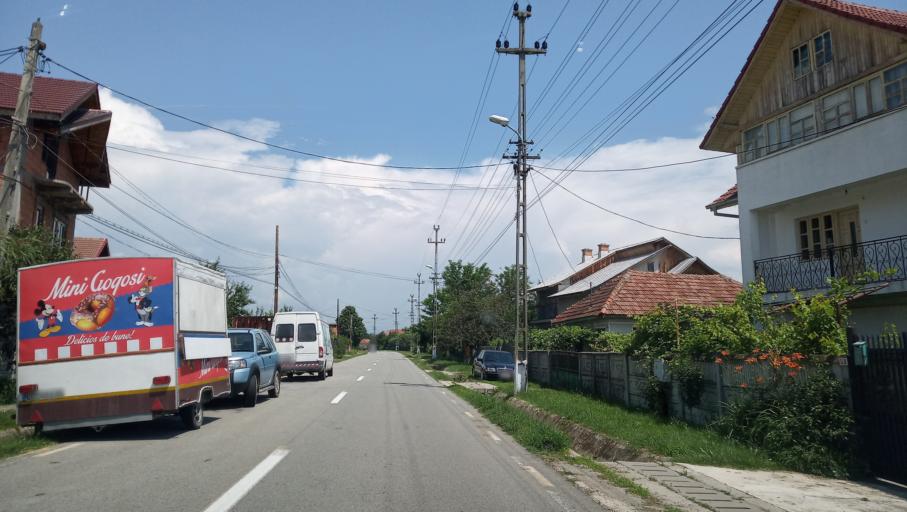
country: RO
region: Gorj
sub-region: Comuna Turcinesti
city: Turcinesti
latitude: 45.0571
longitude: 23.3479
